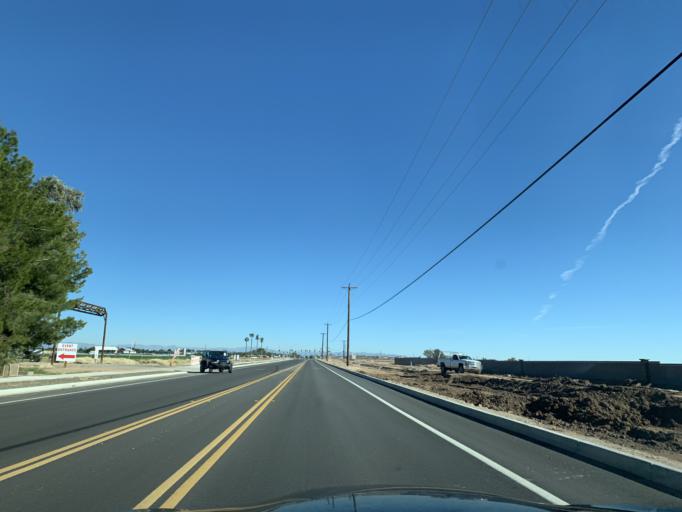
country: US
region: Arizona
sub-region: Maricopa County
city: Queen Creek
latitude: 33.2198
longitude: -111.5908
